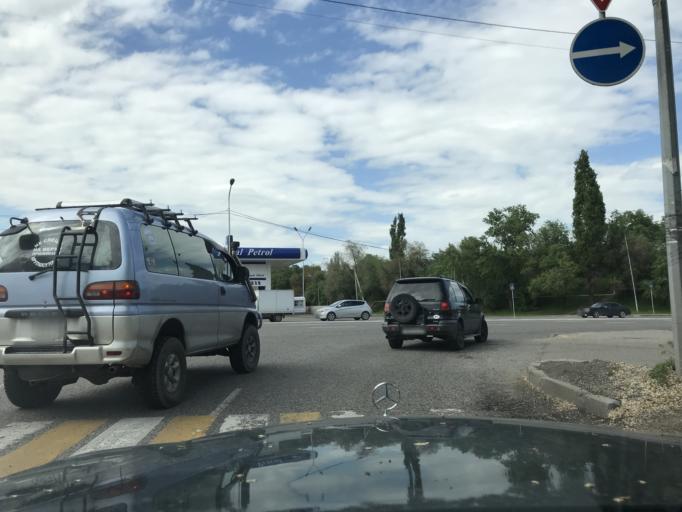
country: KZ
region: Almaty Qalasy
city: Almaty
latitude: 43.2667
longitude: 76.9133
